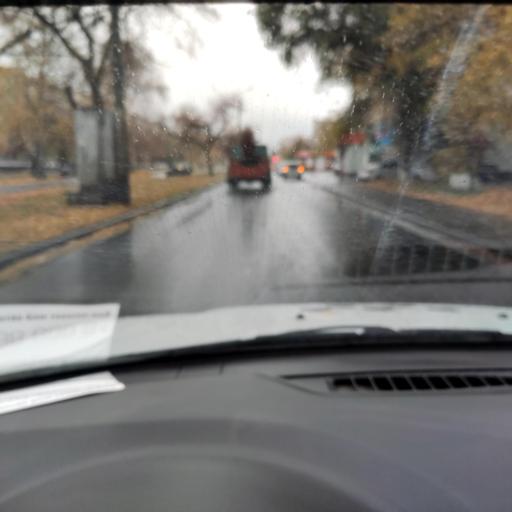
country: RU
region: Samara
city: Tol'yatti
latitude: 53.5202
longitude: 49.4018
